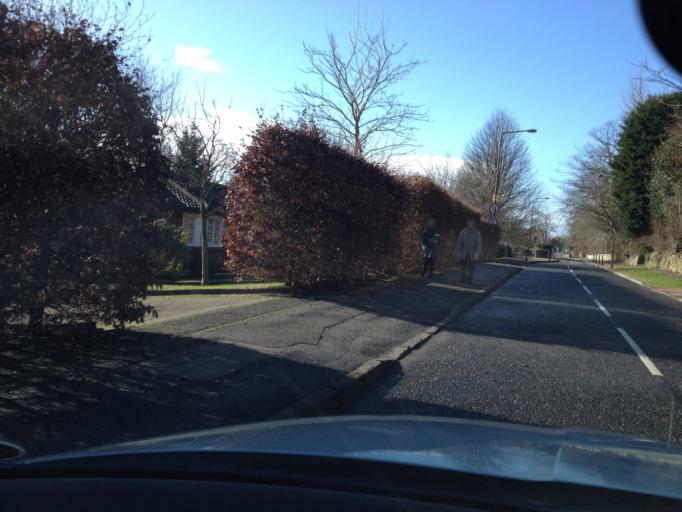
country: GB
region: Scotland
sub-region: West Lothian
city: Livingston
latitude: 55.8869
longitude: -3.5324
